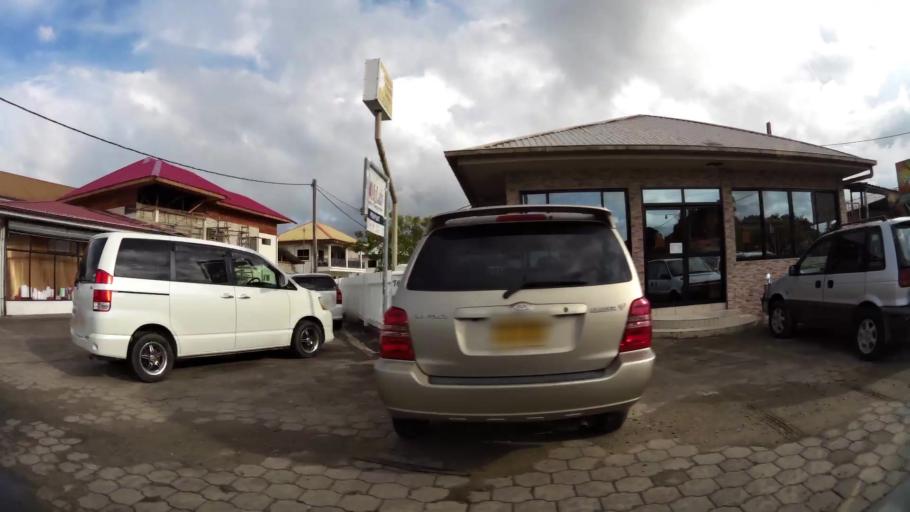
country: SR
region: Paramaribo
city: Paramaribo
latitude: 5.8480
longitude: -55.2459
